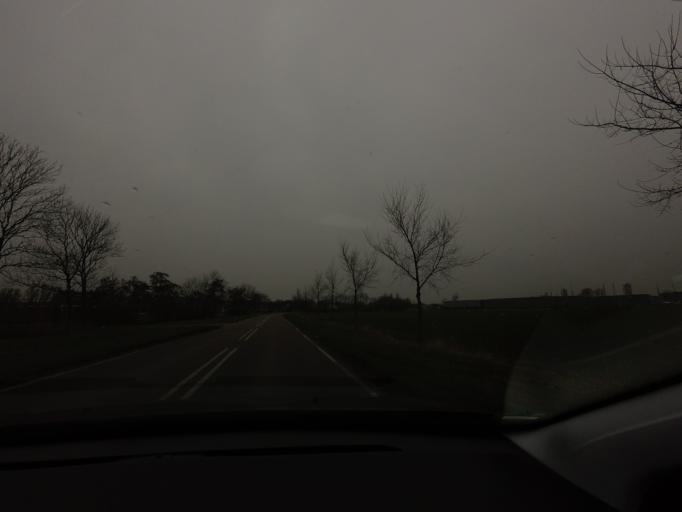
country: NL
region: Friesland
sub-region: Gemeente Franekeradeel
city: Franeker
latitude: 53.1796
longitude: 5.5572
